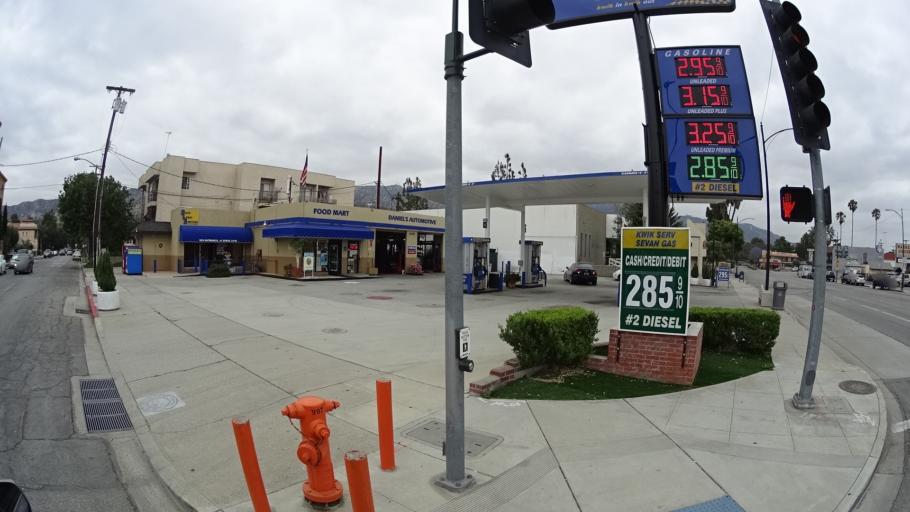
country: US
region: California
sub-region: Los Angeles County
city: Burbank
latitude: 34.1919
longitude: -118.3252
